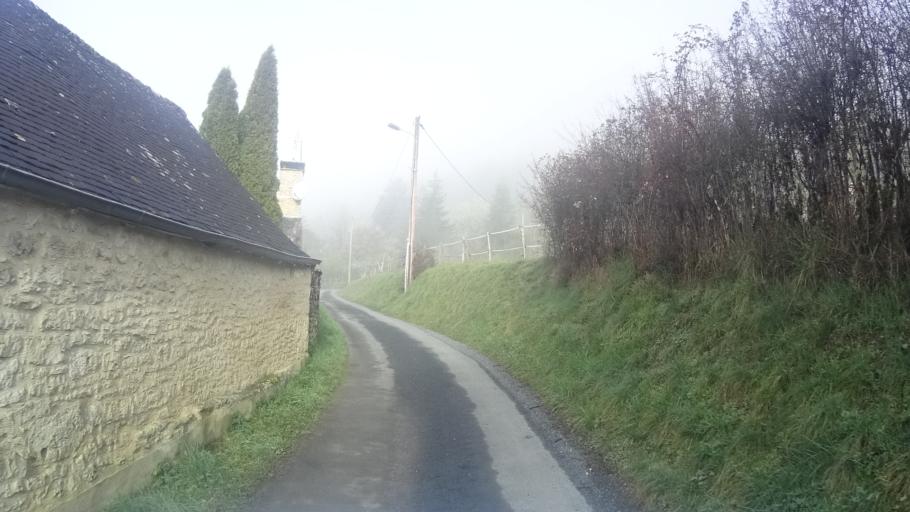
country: FR
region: Aquitaine
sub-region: Departement de la Dordogne
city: Terrasson-Lavilledieu
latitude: 45.0894
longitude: 1.2699
